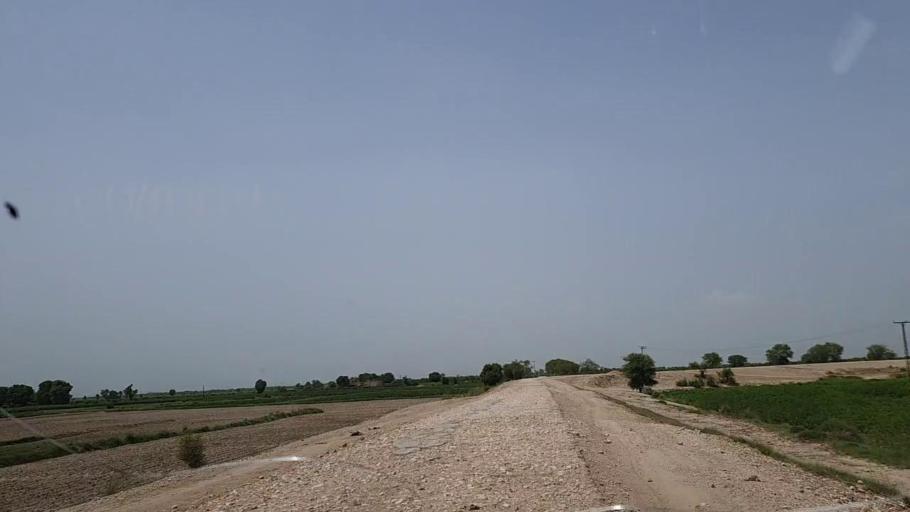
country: PK
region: Sindh
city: Tharu Shah
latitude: 27.0375
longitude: 68.1105
